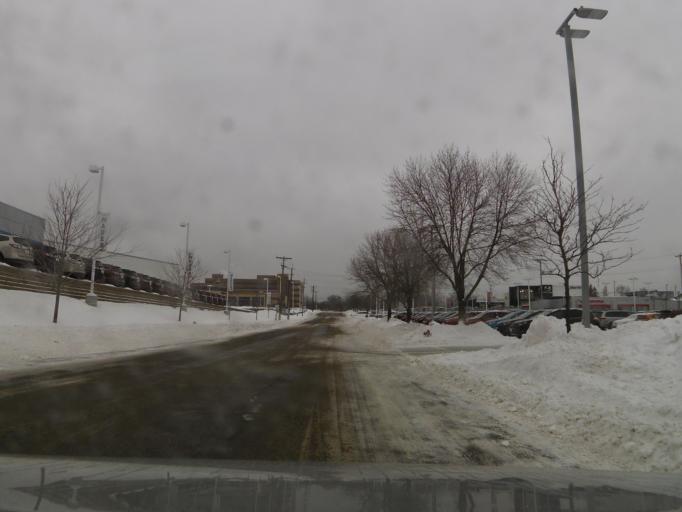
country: US
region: Minnesota
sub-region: Dakota County
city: West Saint Paul
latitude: 44.8812
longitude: -93.0856
